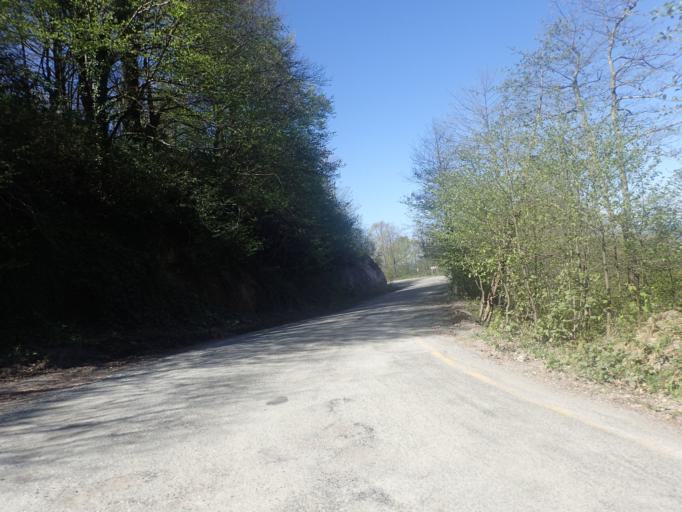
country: TR
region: Ordu
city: Kabaduz
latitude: 40.8112
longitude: 37.9081
